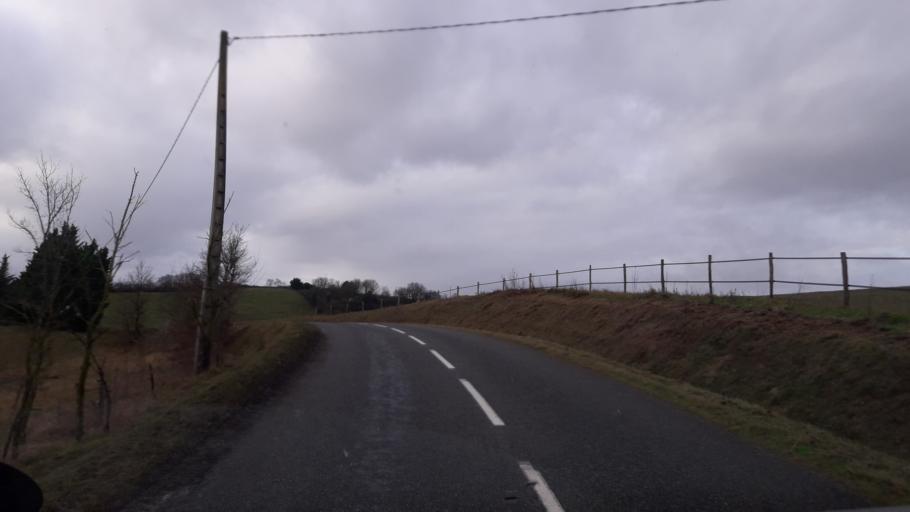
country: FR
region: Midi-Pyrenees
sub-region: Departement de la Haute-Garonne
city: Montesquieu-Volvestre
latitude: 43.2234
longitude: 1.2717
